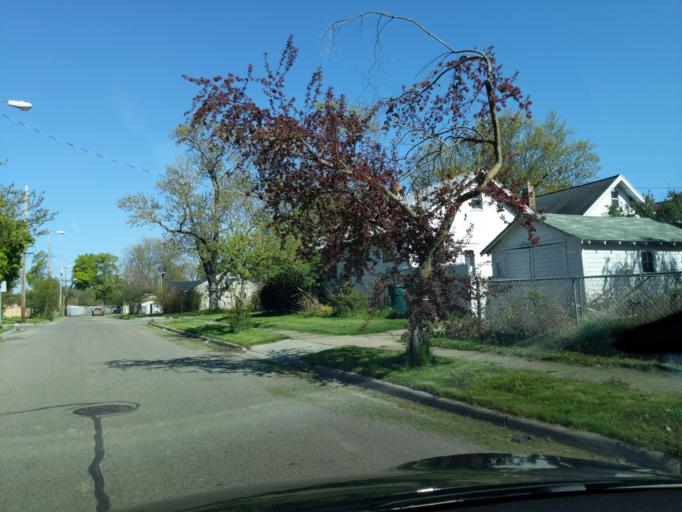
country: US
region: Michigan
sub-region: Ingham County
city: Lansing
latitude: 42.7096
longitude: -84.5623
